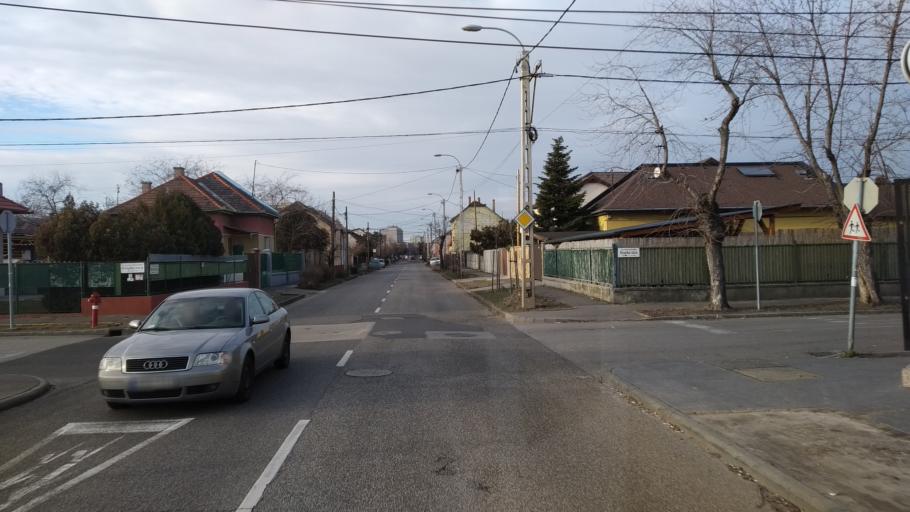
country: HU
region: Budapest
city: Budapest XX. keruelet
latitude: 47.4314
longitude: 19.1162
